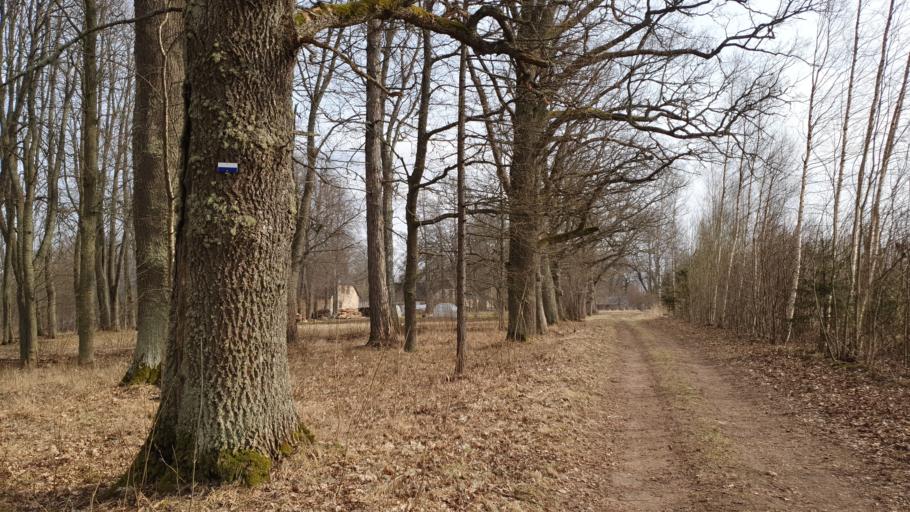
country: LV
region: Beverina
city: Murmuiza
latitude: 57.5493
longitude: 25.5279
